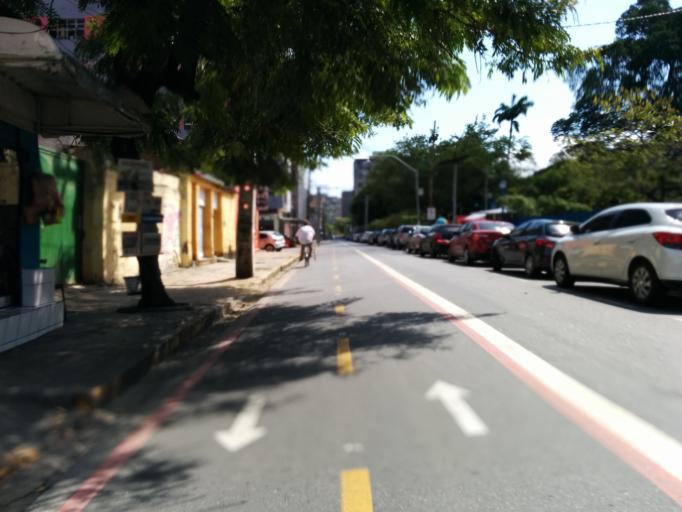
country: BR
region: Pernambuco
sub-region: Recife
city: Recife
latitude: -8.0573
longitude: -34.8803
